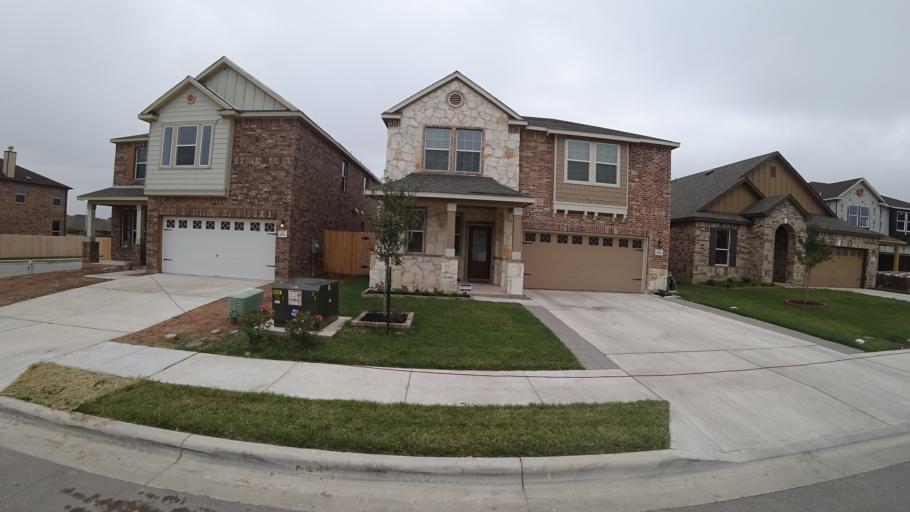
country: US
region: Texas
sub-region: Travis County
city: Pflugerville
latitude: 30.3925
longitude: -97.6469
